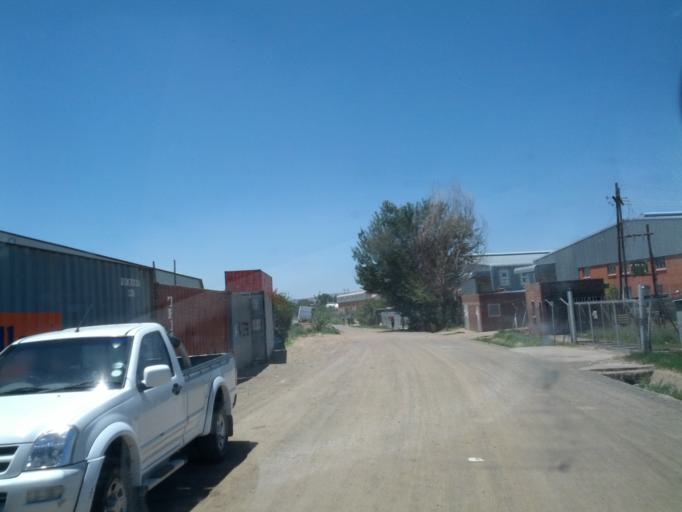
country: LS
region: Maseru
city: Maseru
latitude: -29.2980
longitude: 27.4570
